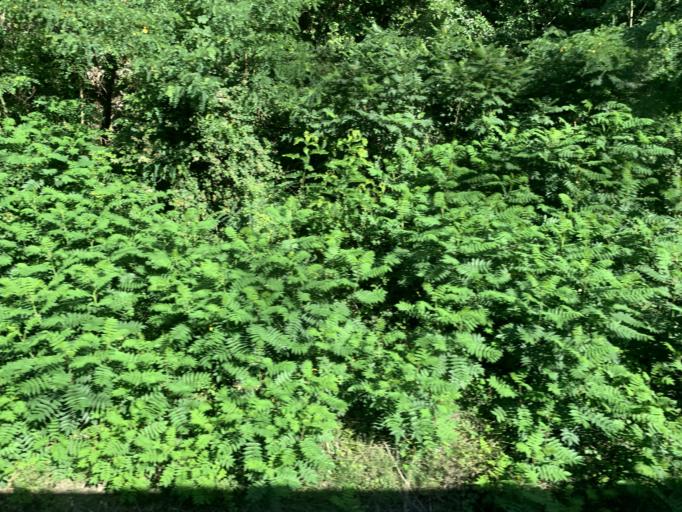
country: FR
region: Rhone-Alpes
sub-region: Departement du Rhone
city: Vernaison
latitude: 45.6416
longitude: 4.8101
